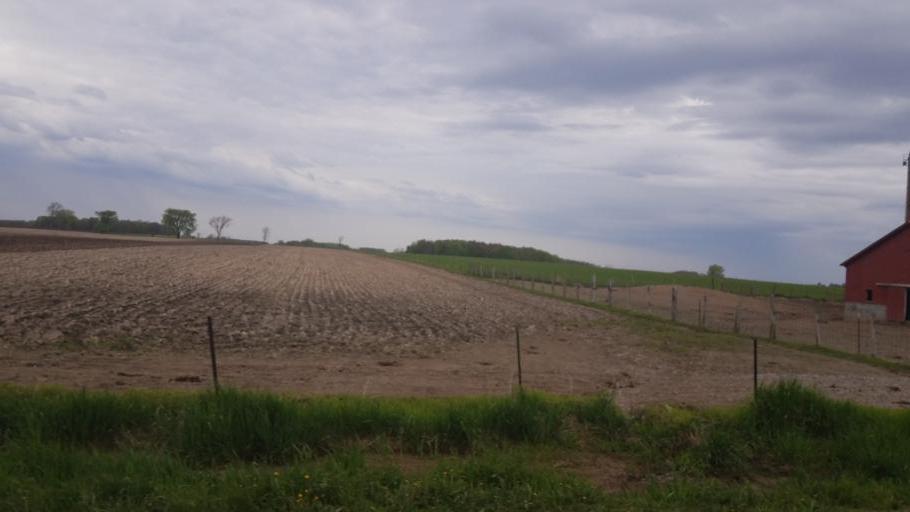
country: US
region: Wisconsin
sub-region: Marathon County
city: Spencer
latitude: 44.6348
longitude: -90.3767
